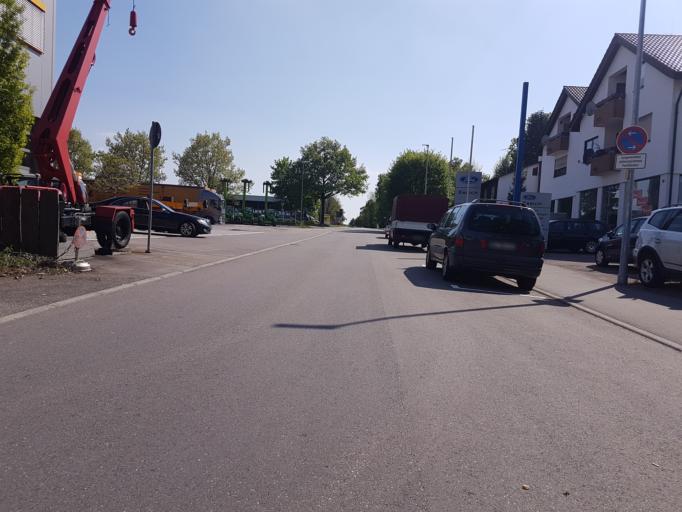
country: DE
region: Baden-Wuerttemberg
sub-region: Regierungsbezirk Stuttgart
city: Bietigheim-Bissingen
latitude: 48.9444
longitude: 9.1384
